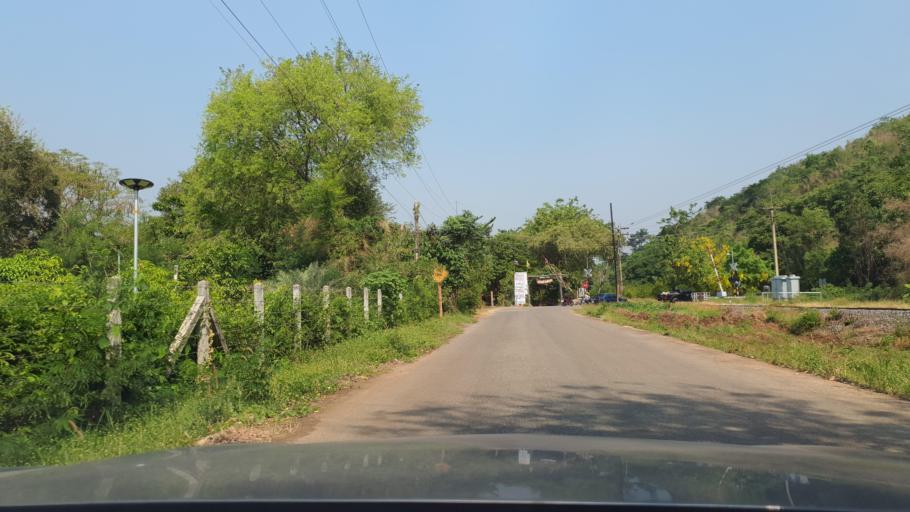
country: TH
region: Kanchanaburi
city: Sai Yok
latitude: 14.0955
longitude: 99.1757
